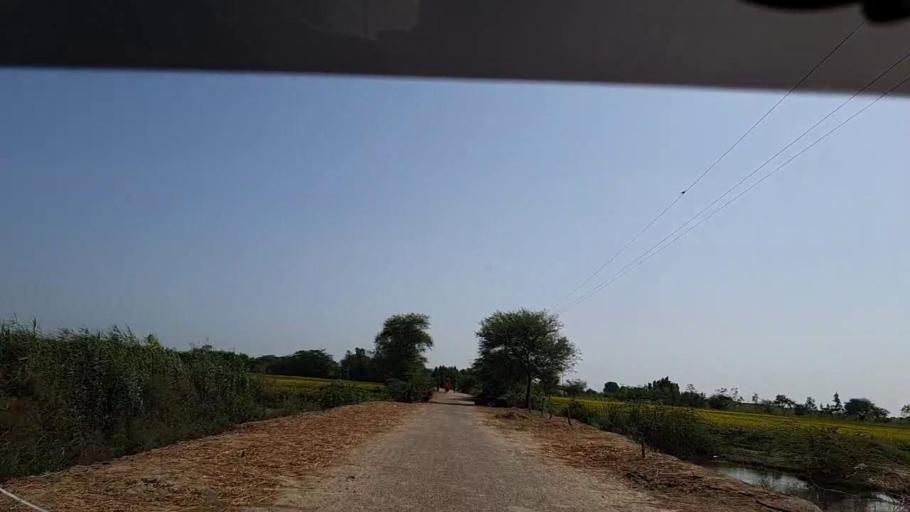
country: PK
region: Sindh
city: Badin
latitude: 24.6367
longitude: 68.7867
